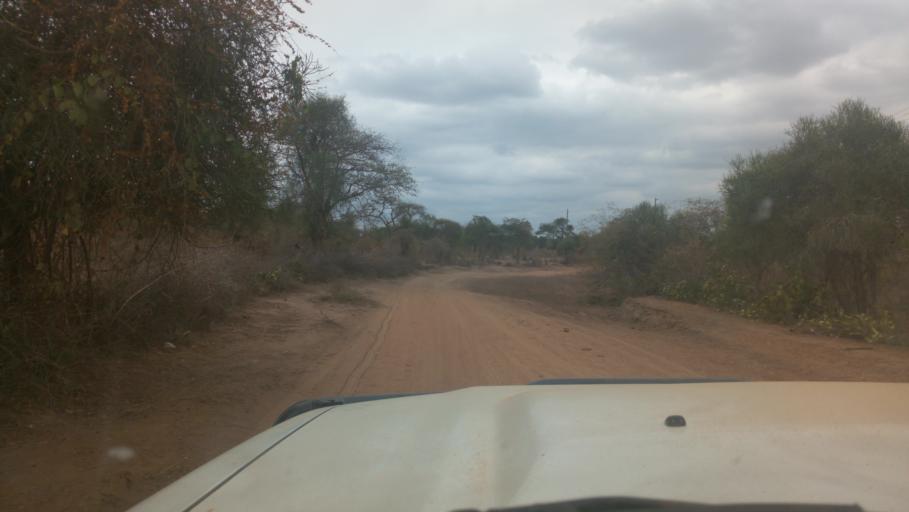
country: KE
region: Kitui
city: Kitui
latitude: -1.5946
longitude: 37.9050
